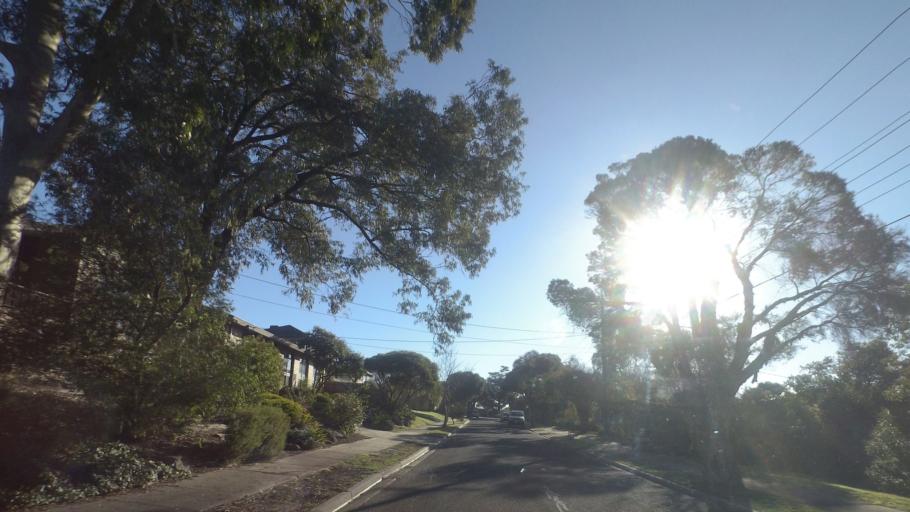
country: AU
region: Victoria
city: Macleod
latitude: -37.7312
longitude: 145.0633
